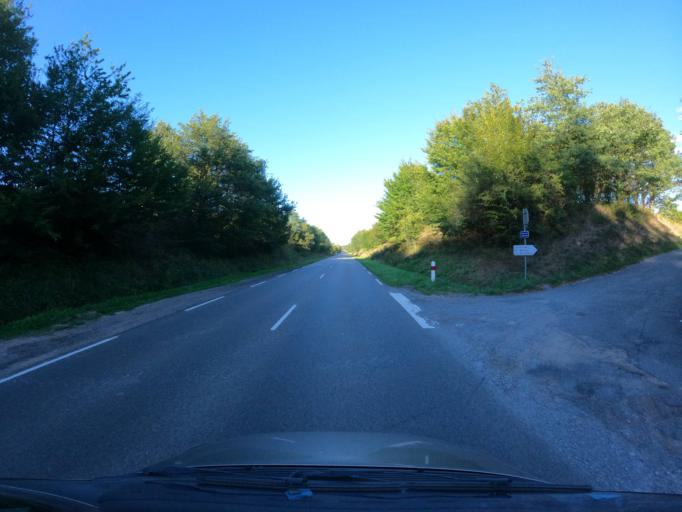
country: FR
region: Bourgogne
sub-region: Departement de Saone-et-Loire
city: Saint-Eusebe
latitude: 46.7152
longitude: 4.4250
